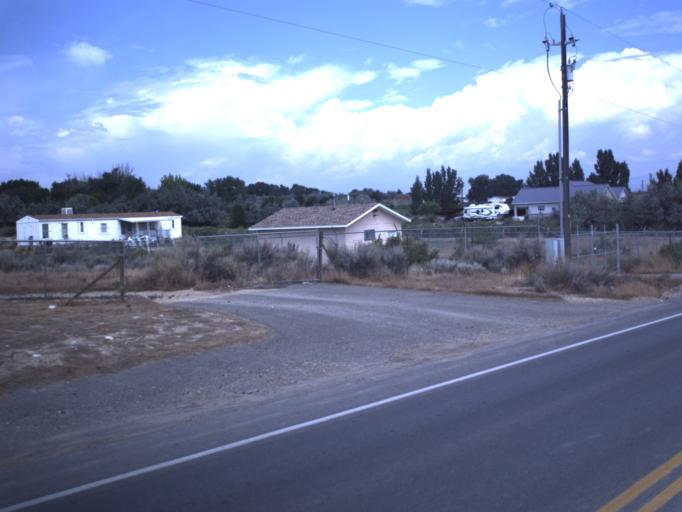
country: US
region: Utah
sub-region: Uintah County
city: Naples
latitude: 40.3715
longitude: -109.4983
